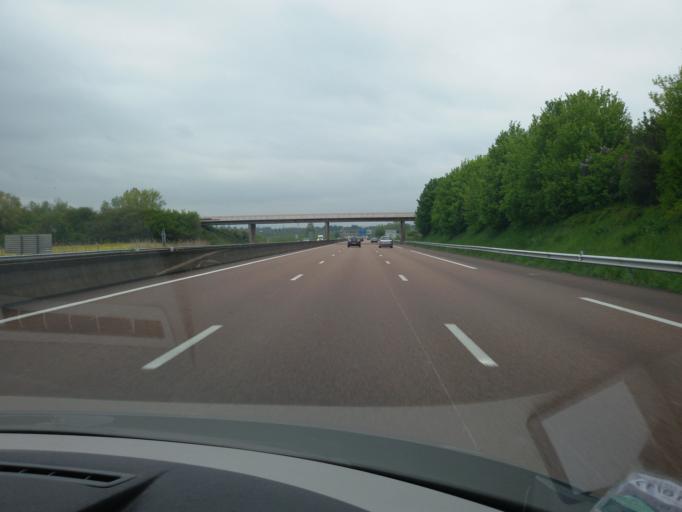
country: FR
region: Bourgogne
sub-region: Departement de Saone-et-Loire
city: Sevrey
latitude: 46.7404
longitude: 4.8344
